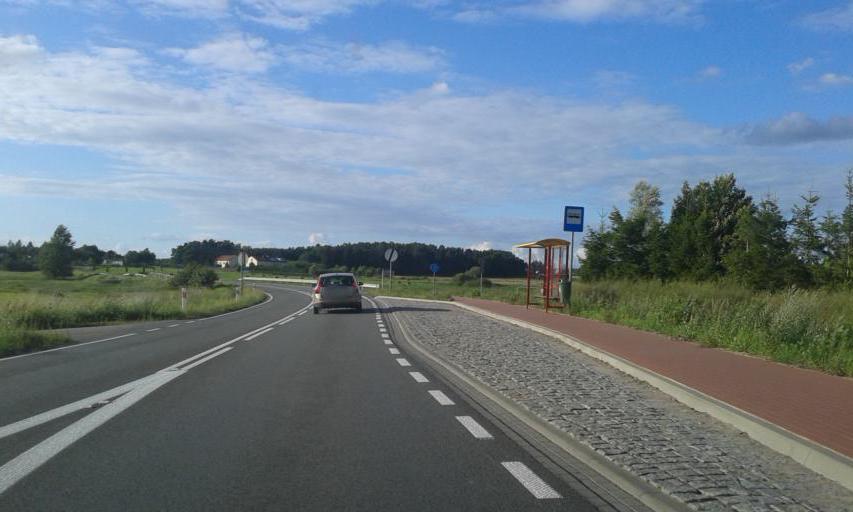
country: PL
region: West Pomeranian Voivodeship
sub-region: Koszalin
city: Koszalin
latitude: 54.1344
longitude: 16.1722
